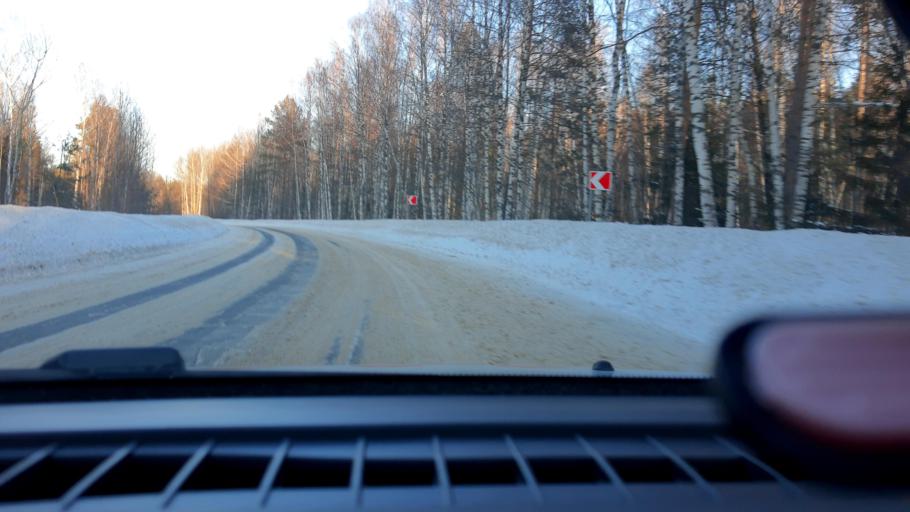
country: RU
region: Nizjnij Novgorod
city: Pervoye Maya
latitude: 56.2175
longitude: 44.5993
